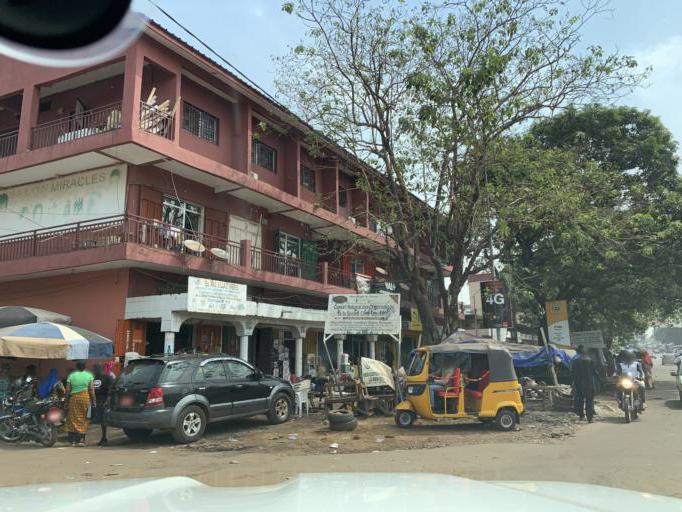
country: GN
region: Conakry
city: Conakry
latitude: 9.5481
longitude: -13.6742
